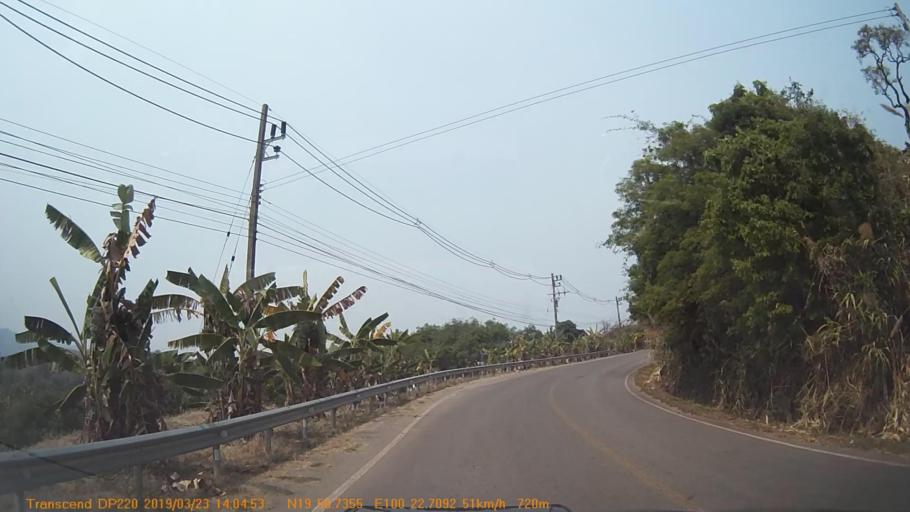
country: TH
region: Chiang Rai
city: Khun Tan
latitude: 19.8457
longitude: 100.3786
